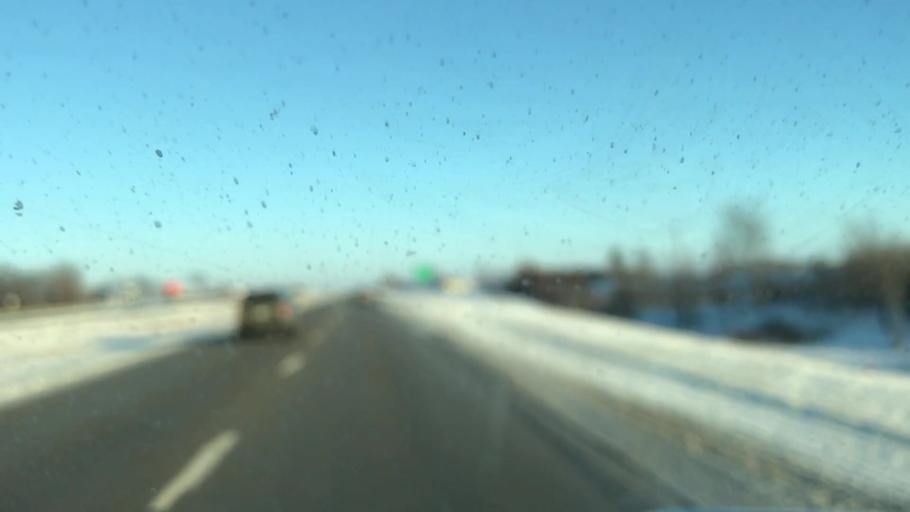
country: US
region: Missouri
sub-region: Andrew County
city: Country Club Village
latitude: 39.7476
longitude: -94.6982
